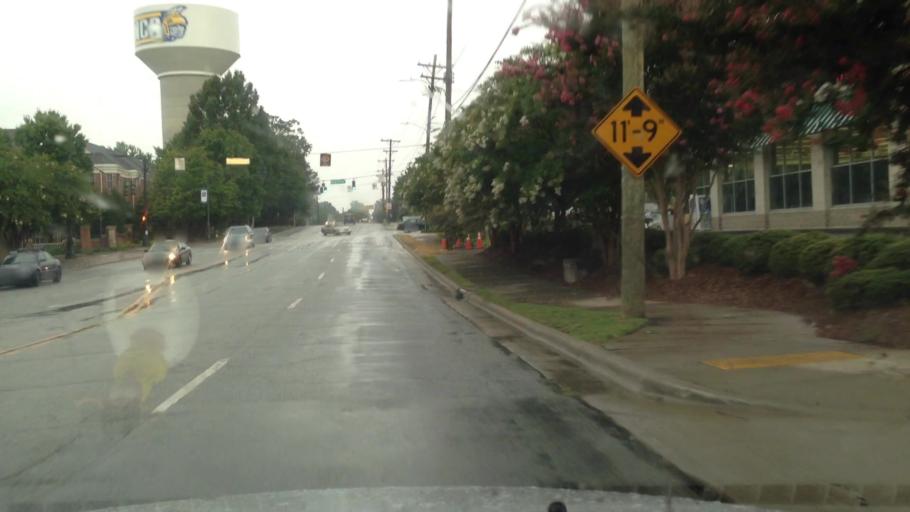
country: US
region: North Carolina
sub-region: Guilford County
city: Greensboro
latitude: 36.0656
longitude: -79.8154
